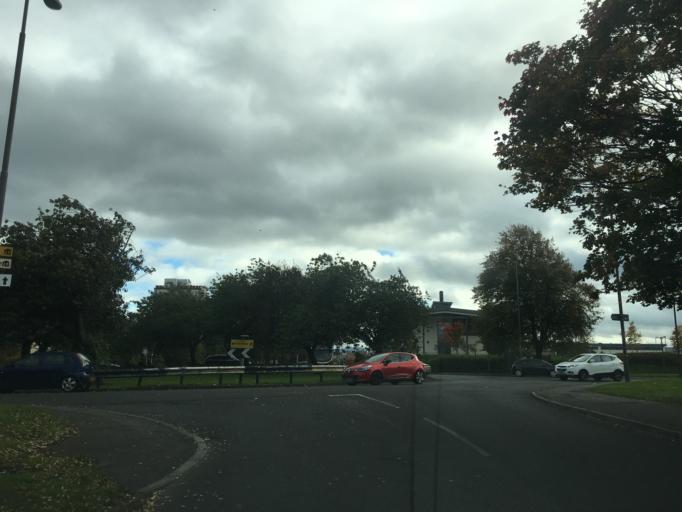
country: GB
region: Scotland
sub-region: Edinburgh
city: Edinburgh
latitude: 55.9754
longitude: -3.2541
